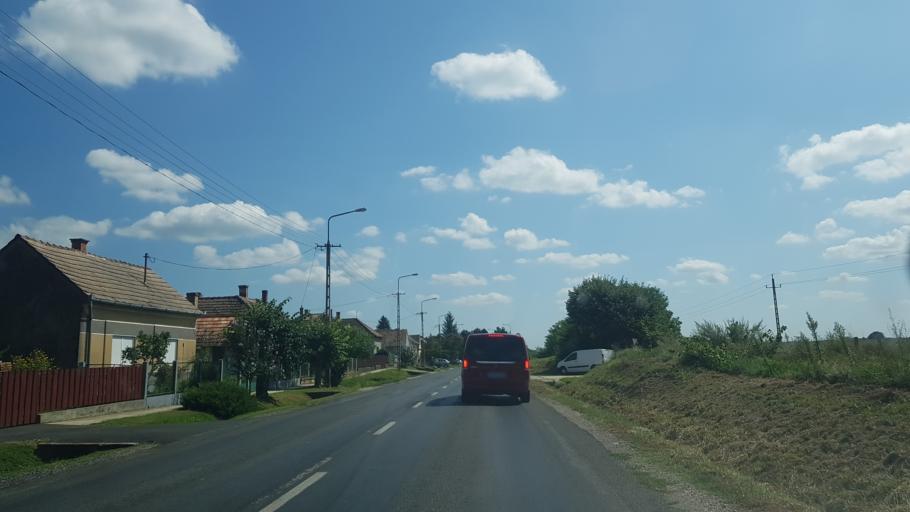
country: HU
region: Somogy
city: Marcali
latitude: 46.5458
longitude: 17.4129
